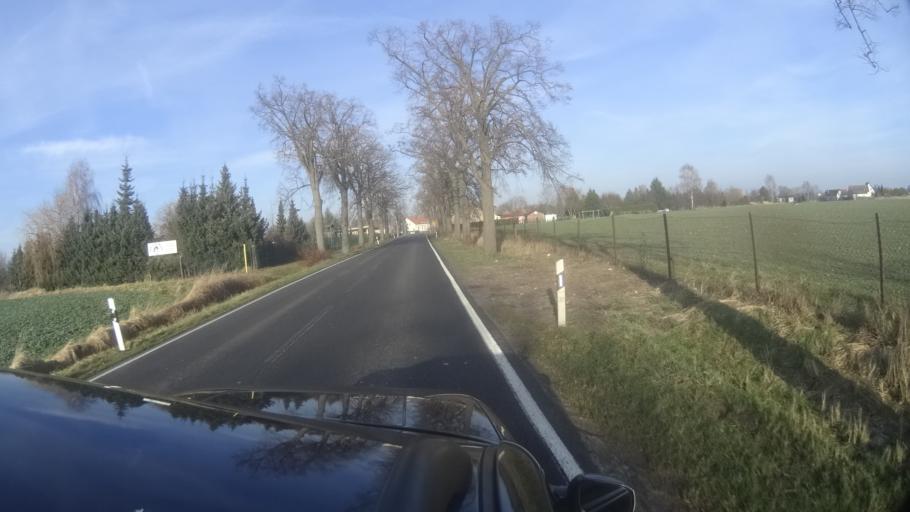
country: DE
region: Brandenburg
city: Velten
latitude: 52.7123
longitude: 13.1024
